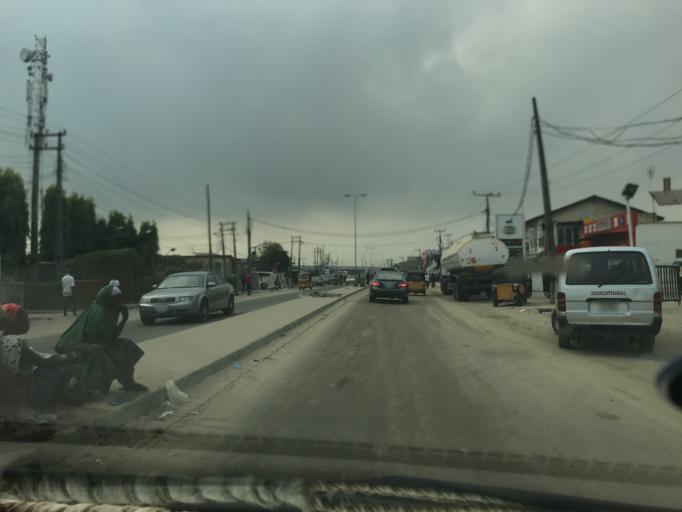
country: NG
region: Lagos
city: Ikoyi
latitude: 6.4712
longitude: 3.5654
